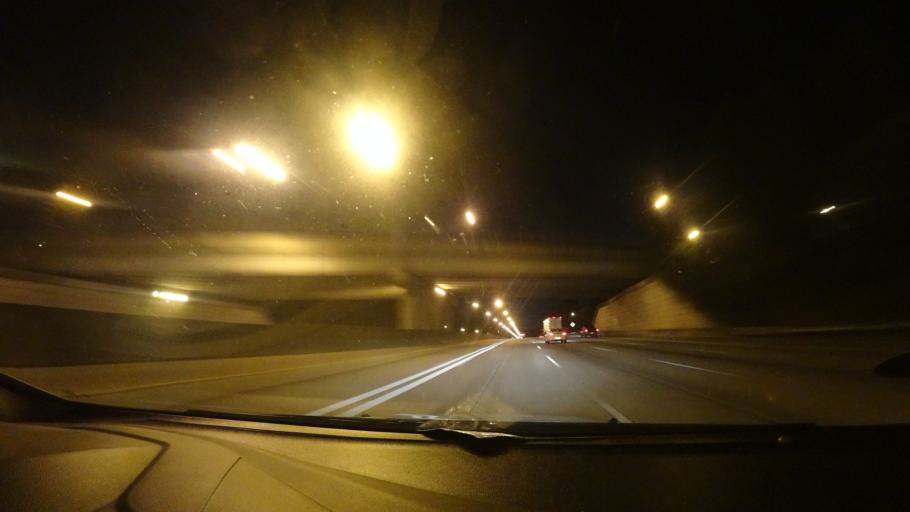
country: US
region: Georgia
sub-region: DeKalb County
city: Gresham Park
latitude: 33.7158
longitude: -84.3100
